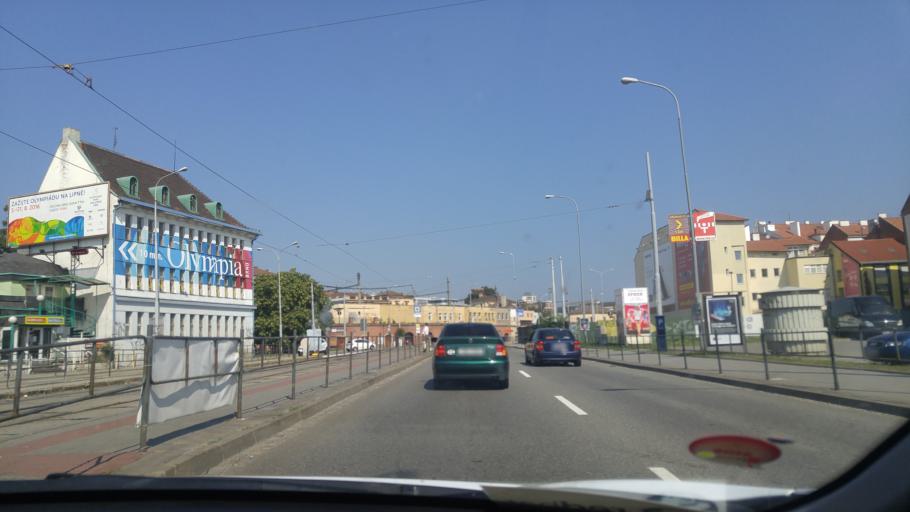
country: CZ
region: South Moravian
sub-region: Mesto Brno
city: Brno
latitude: 49.1898
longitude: 16.6148
